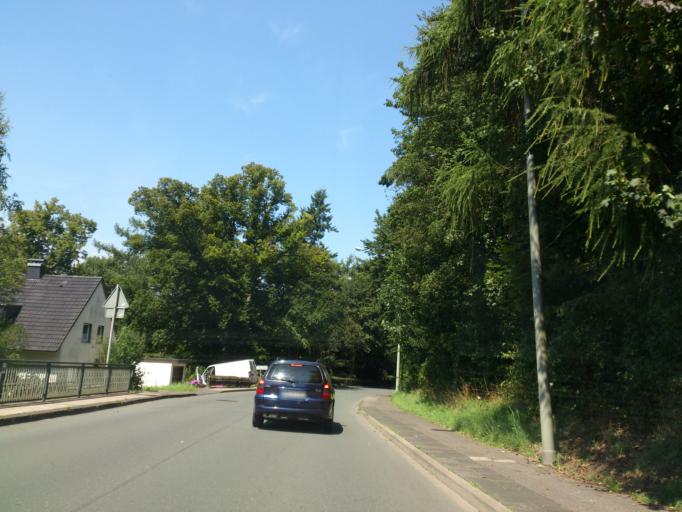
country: DE
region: North Rhine-Westphalia
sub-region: Regierungsbezirk Detmold
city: Altenbeken
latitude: 51.7590
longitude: 8.9520
